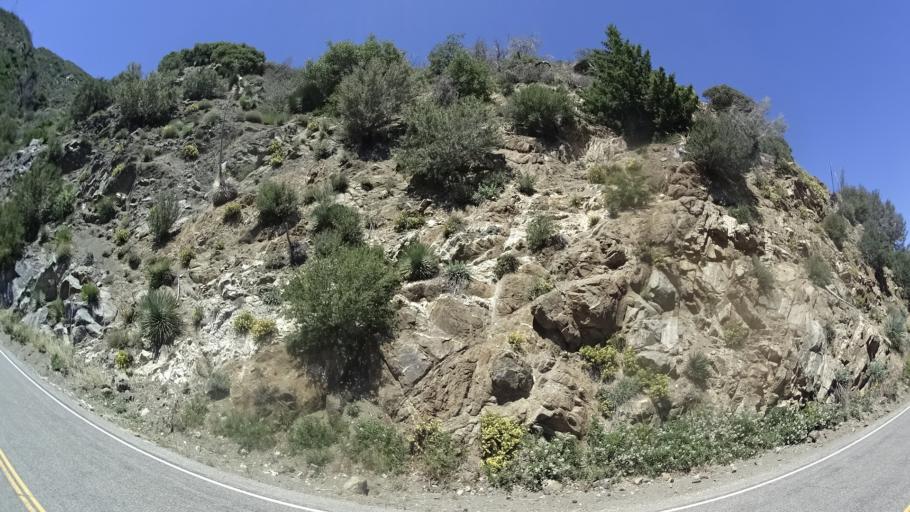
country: US
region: California
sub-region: Los Angeles County
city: Altadena
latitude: 34.2666
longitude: -118.0842
